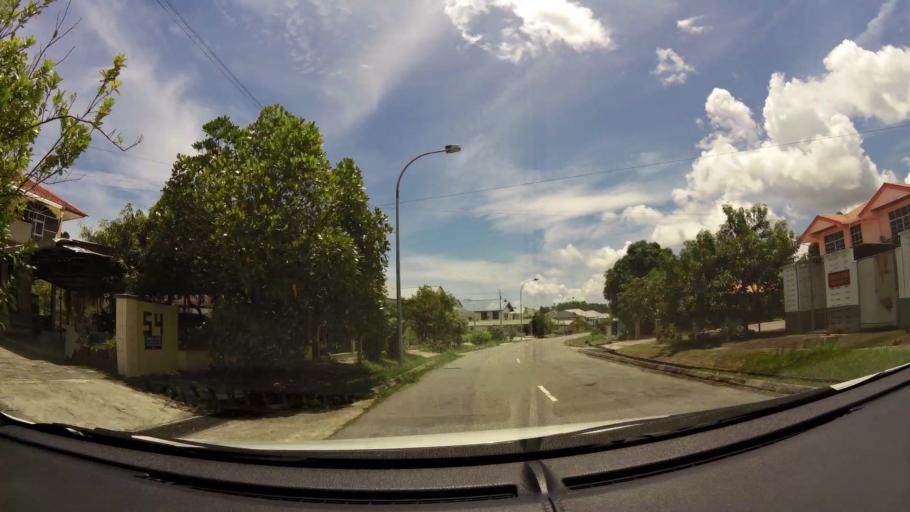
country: BN
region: Brunei and Muara
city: Bandar Seri Begawan
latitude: 4.9634
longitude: 114.9113
